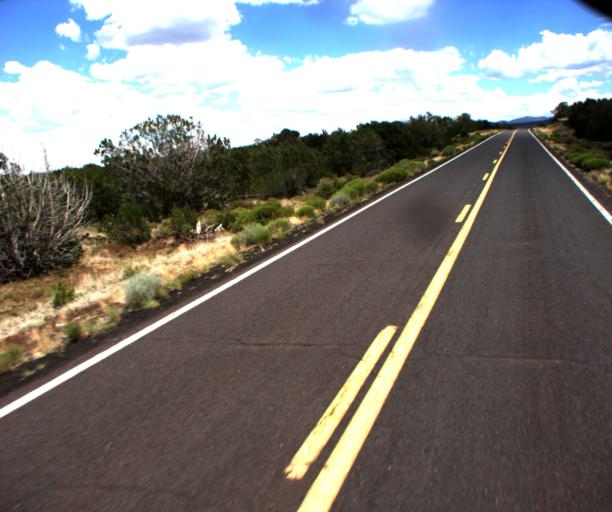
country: US
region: Arizona
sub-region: Coconino County
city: Parks
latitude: 35.5554
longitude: -111.8713
